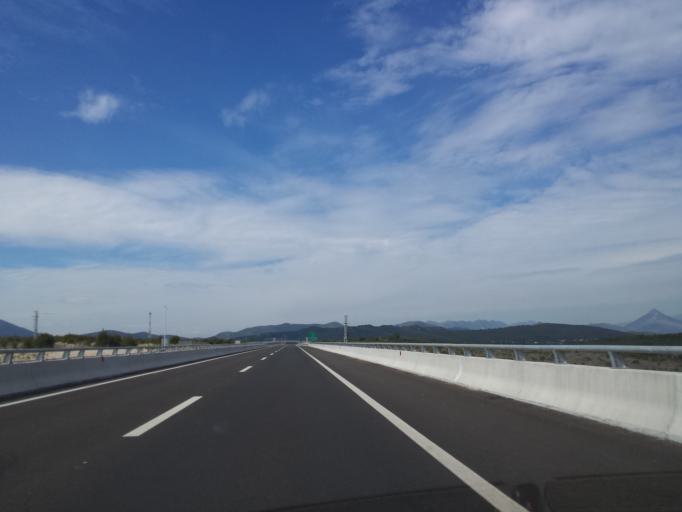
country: BA
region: Federation of Bosnia and Herzegovina
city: Capljina
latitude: 43.1527
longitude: 17.6171
